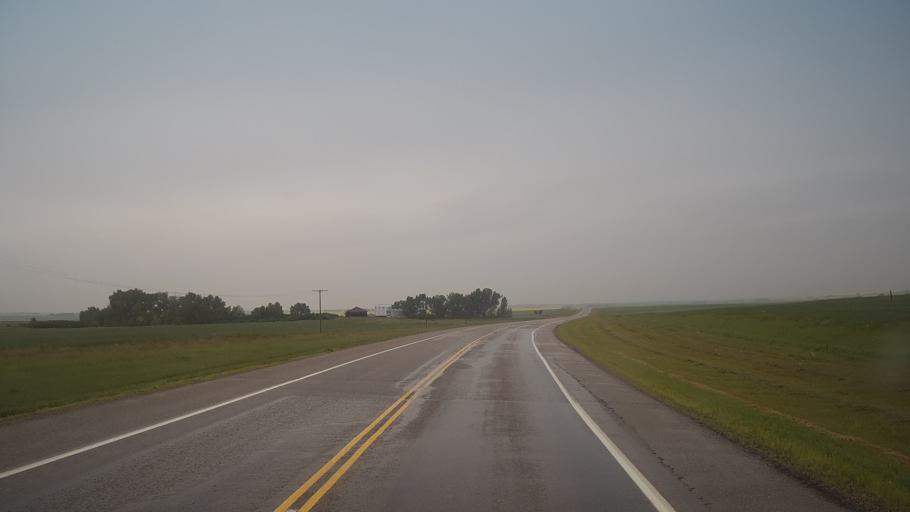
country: CA
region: Saskatchewan
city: Wilkie
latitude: 52.2033
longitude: -108.4730
